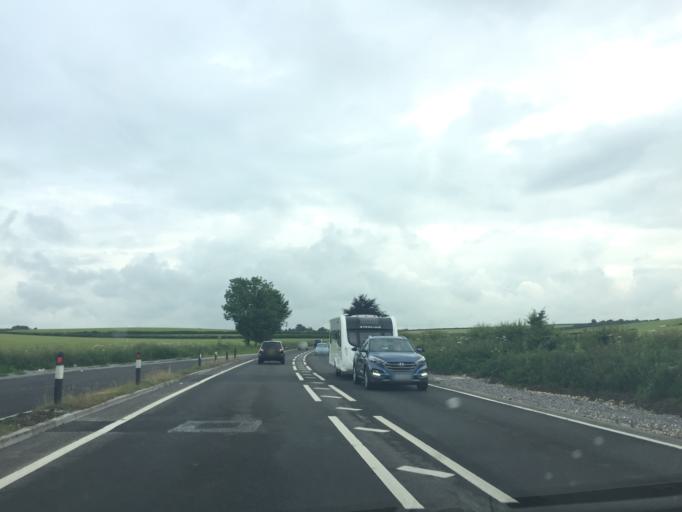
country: GB
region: England
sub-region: Dorset
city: Bovington Camp
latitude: 50.7610
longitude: -2.2090
